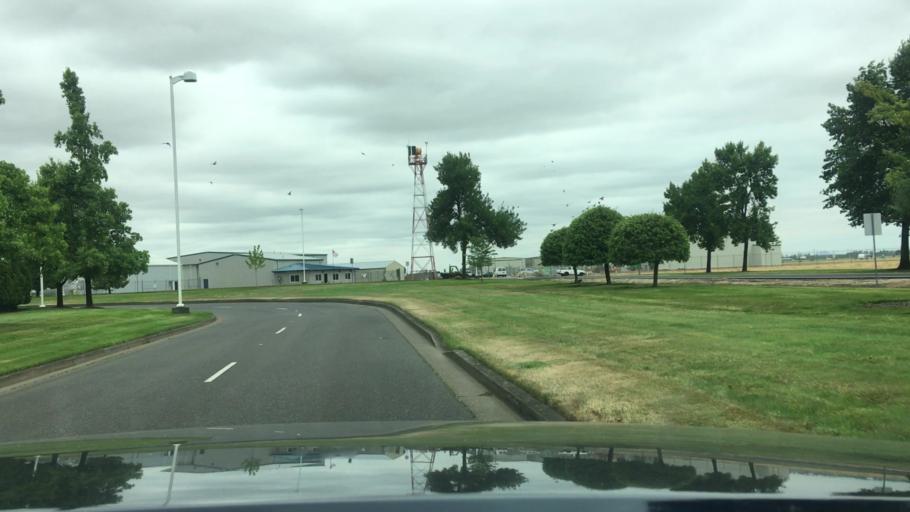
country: US
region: Oregon
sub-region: Lane County
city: Junction City
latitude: 44.1200
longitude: -123.2089
